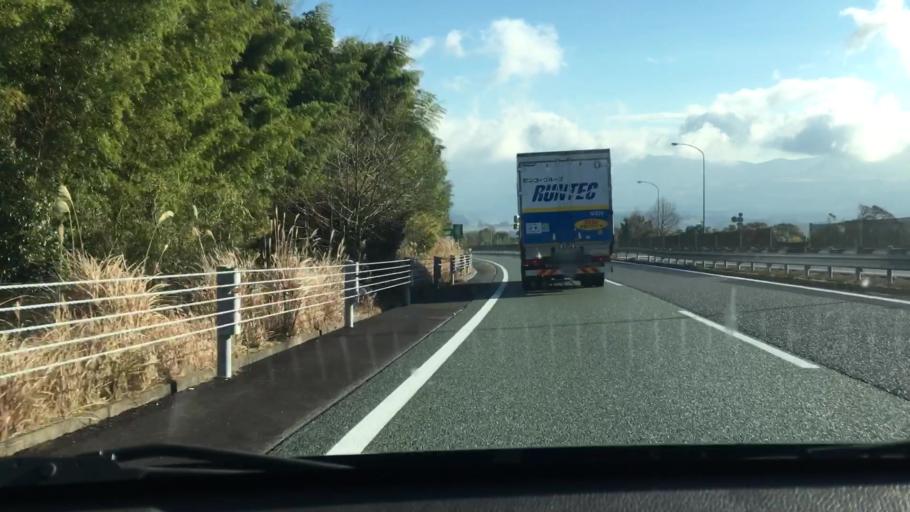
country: JP
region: Kumamoto
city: Hitoyoshi
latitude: 32.0723
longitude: 130.7937
